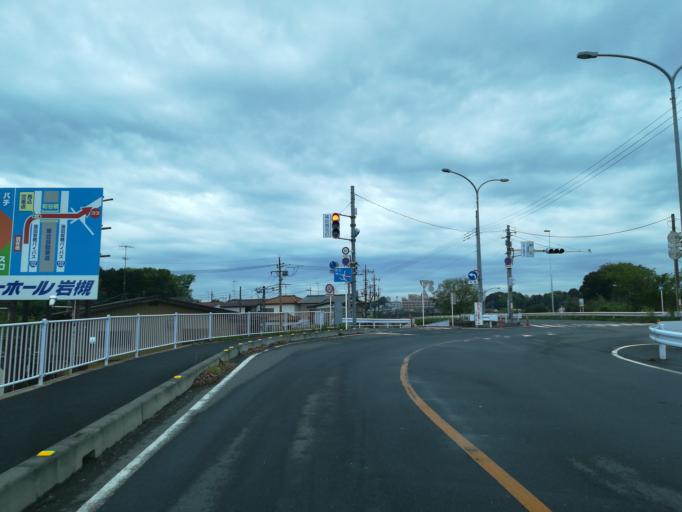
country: JP
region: Saitama
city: Hasuda
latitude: 35.9712
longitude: 139.6678
